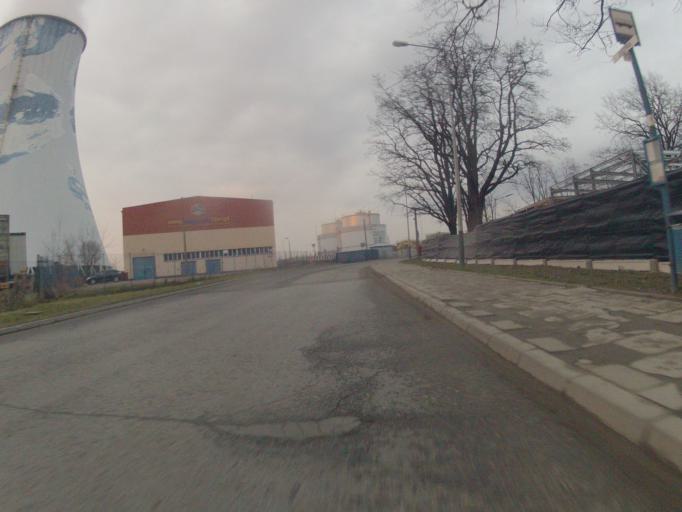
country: PL
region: Lesser Poland Voivodeship
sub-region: Powiat wielicki
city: Czarnochowice
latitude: 50.0512
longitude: 20.0147
